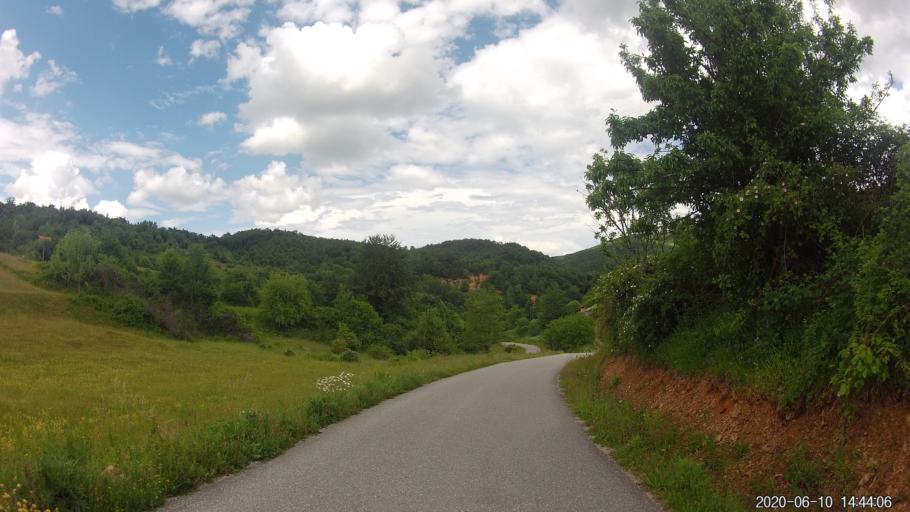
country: XK
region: Prizren
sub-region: Komuna e Therandes
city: Budakovo
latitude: 42.3816
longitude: 20.9443
